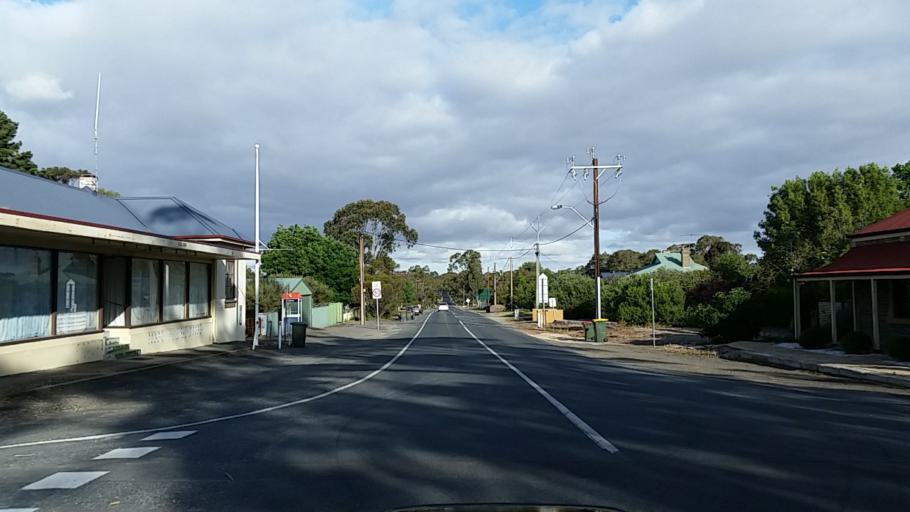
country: AU
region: South Australia
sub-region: Barossa
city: Angaston
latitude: -34.5546
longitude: 139.1340
